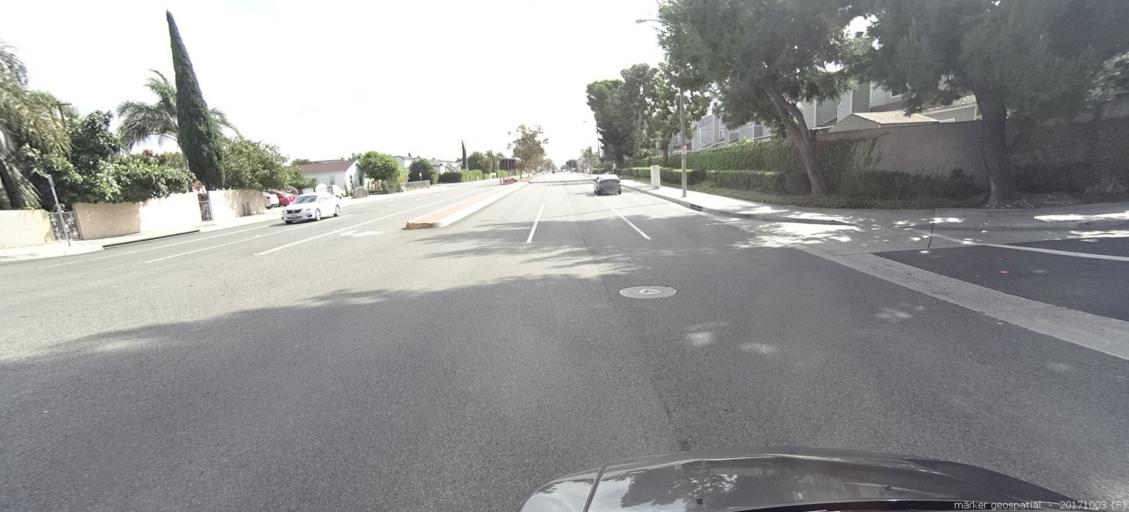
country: US
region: California
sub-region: Orange County
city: Garden Grove
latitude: 33.7596
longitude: -117.9345
